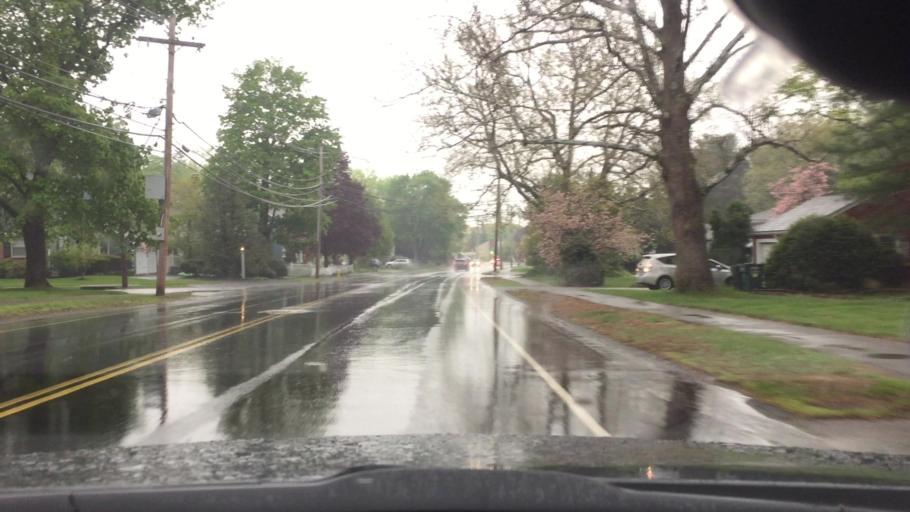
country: US
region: Massachusetts
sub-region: Norfolk County
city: Needham
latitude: 42.2718
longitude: -71.2083
